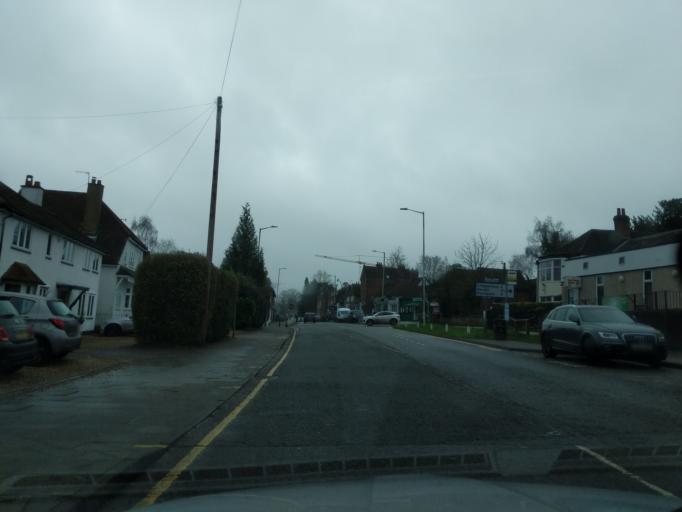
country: GB
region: England
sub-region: Hertfordshire
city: Kings Langley
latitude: 51.7146
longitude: -0.4506
